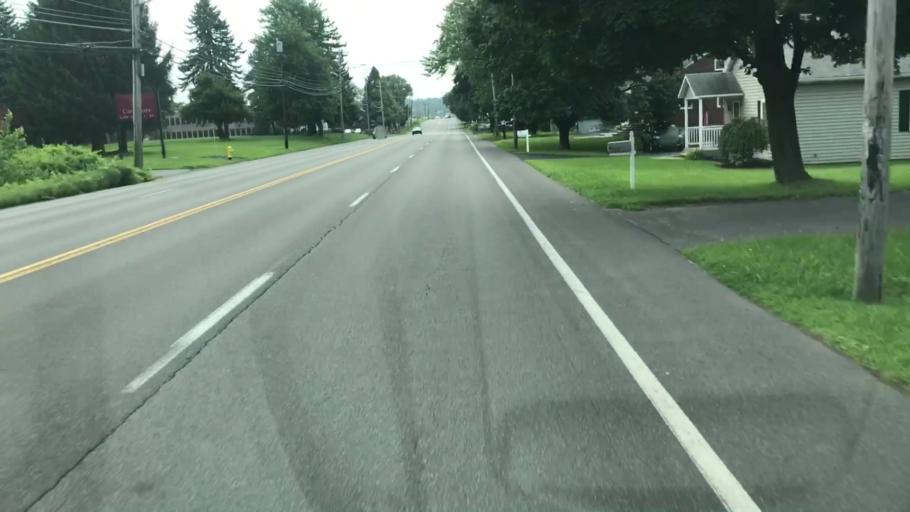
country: US
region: New York
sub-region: Onondaga County
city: Galeville
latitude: 43.0961
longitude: -76.1771
